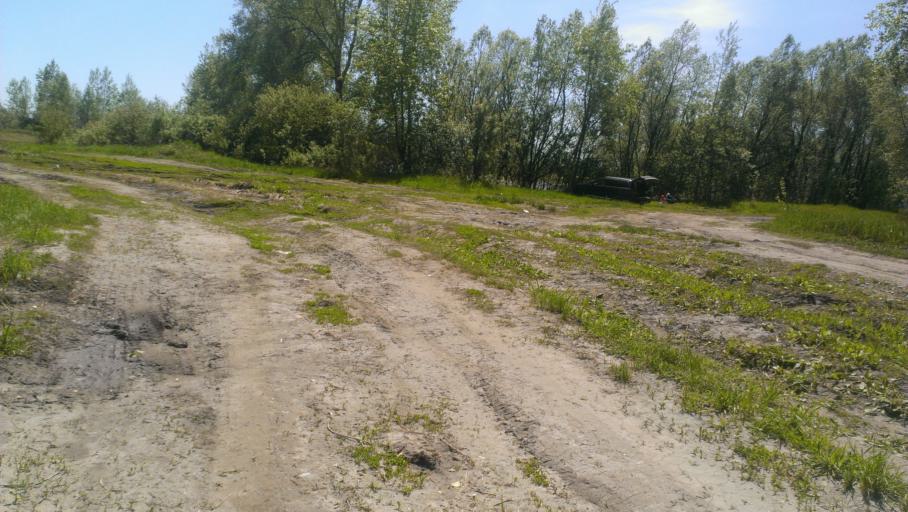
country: RU
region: Altai Krai
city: Zaton
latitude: 53.3133
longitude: 83.8523
